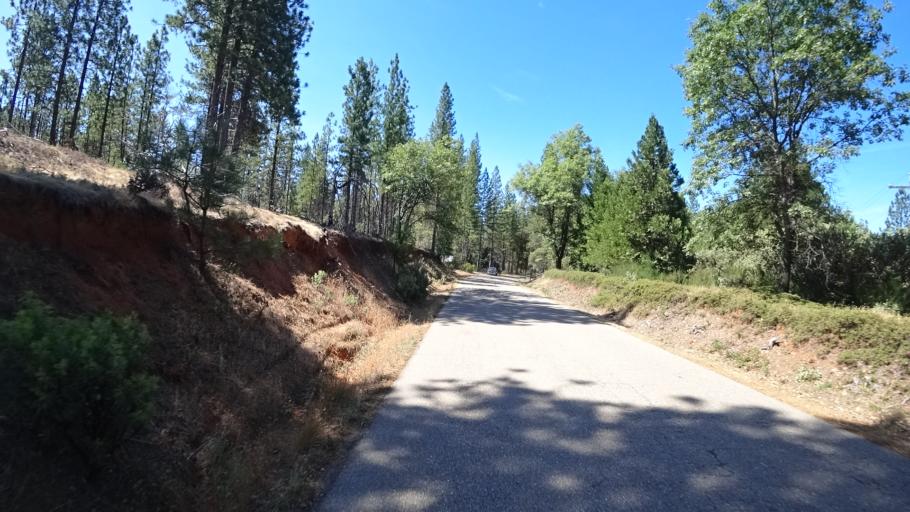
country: US
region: California
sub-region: Amador County
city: Pioneer
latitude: 38.4110
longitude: -120.5026
